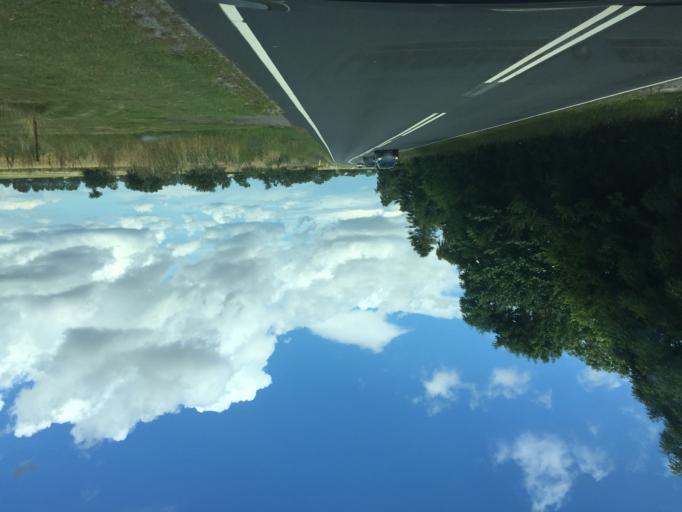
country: DK
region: South Denmark
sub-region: Nordfyns Kommune
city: Otterup
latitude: 55.4730
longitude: 10.3502
